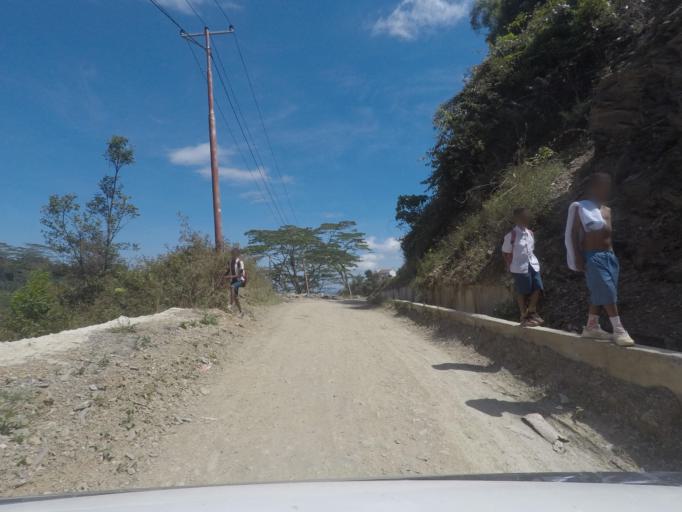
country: TL
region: Ermera
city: Gleno
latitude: -8.7526
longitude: 125.3282
